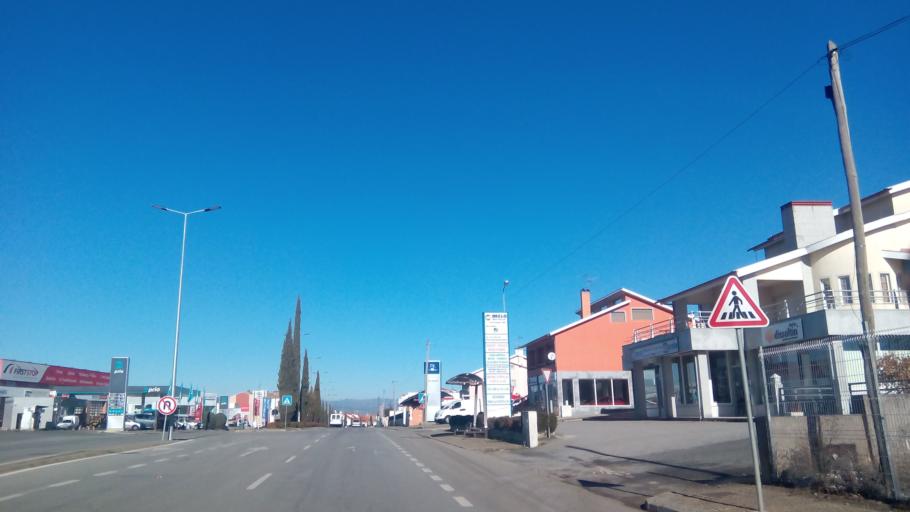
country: PT
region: Braganca
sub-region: Braganca Municipality
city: Braganca
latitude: 41.7799
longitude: -6.7789
